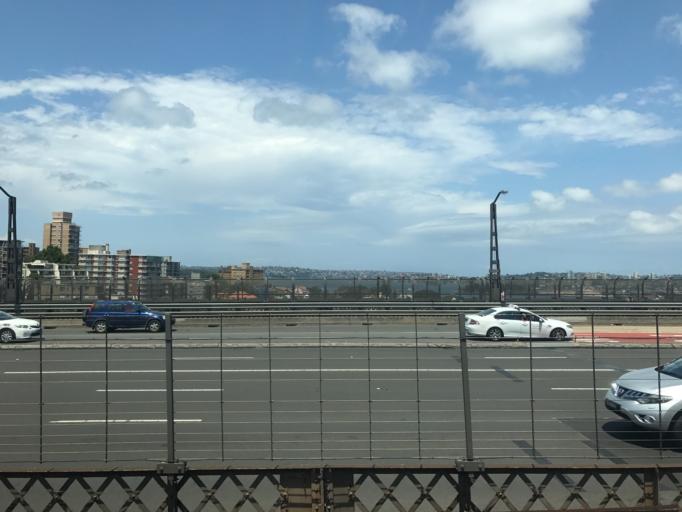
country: AU
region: New South Wales
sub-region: North Sydney
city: Milsons Point
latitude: -33.8494
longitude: 151.2124
